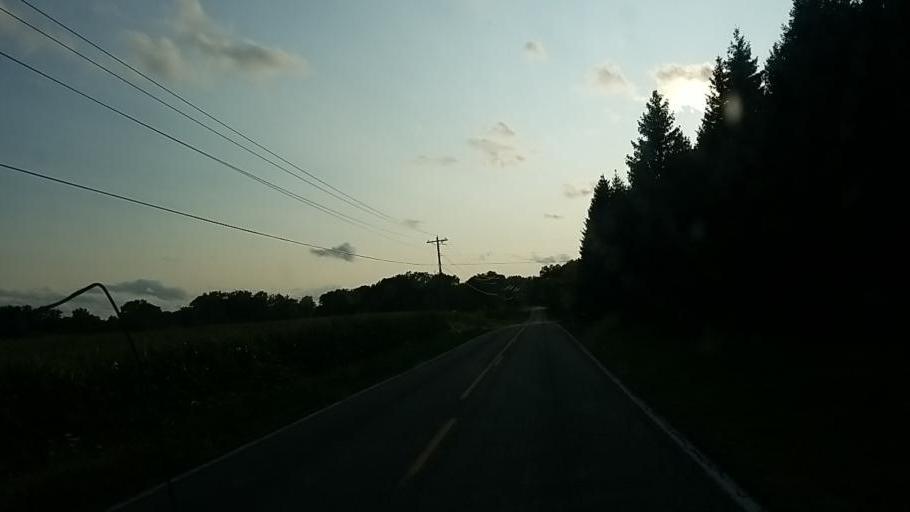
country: US
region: Michigan
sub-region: Montcalm County
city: Lakeview
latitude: 43.3593
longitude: -85.3488
